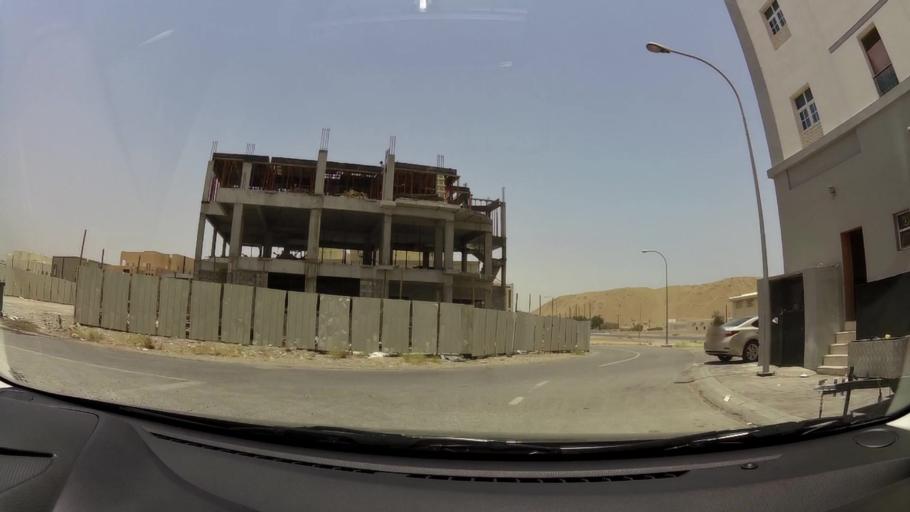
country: OM
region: Muhafazat Masqat
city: Bawshar
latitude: 23.5635
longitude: 58.4226
